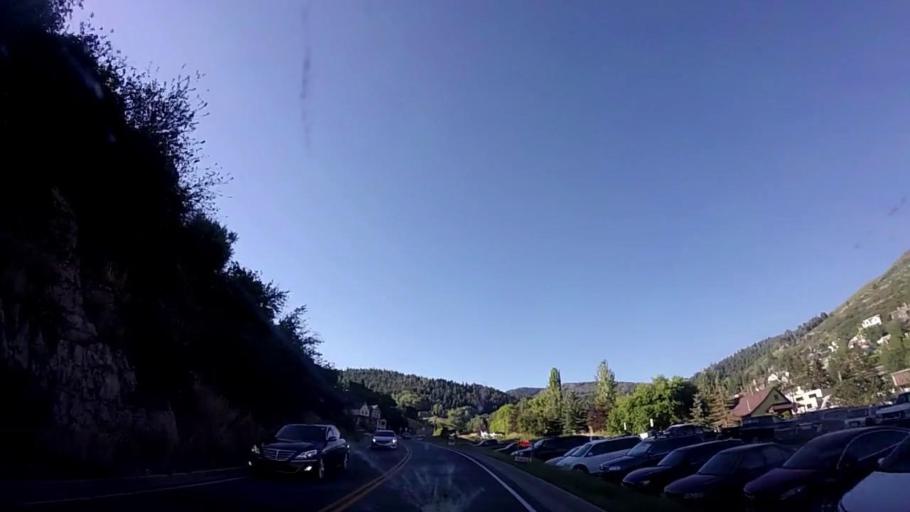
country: US
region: Utah
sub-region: Summit County
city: Park City
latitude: 40.6423
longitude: -111.4935
